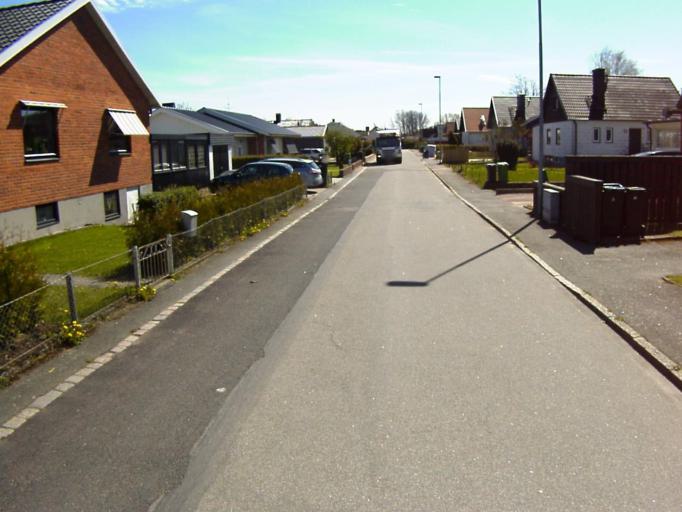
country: SE
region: Skane
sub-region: Kristianstads Kommun
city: Kristianstad
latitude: 56.0104
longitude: 14.1531
